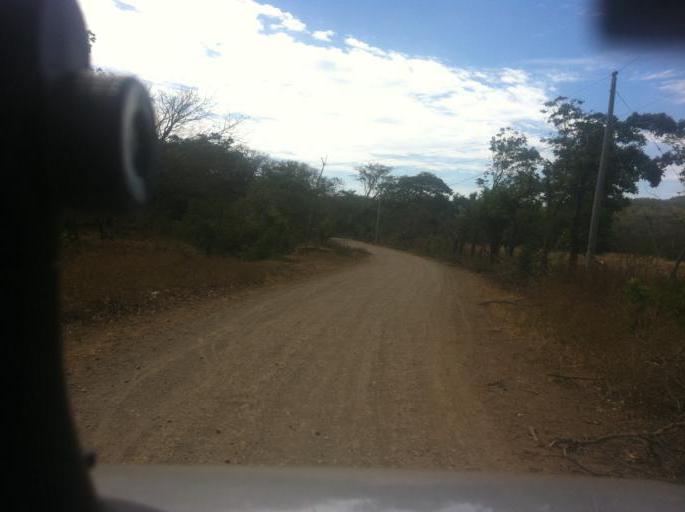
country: NI
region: Rivas
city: Belen
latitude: 11.5849
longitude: -86.0244
